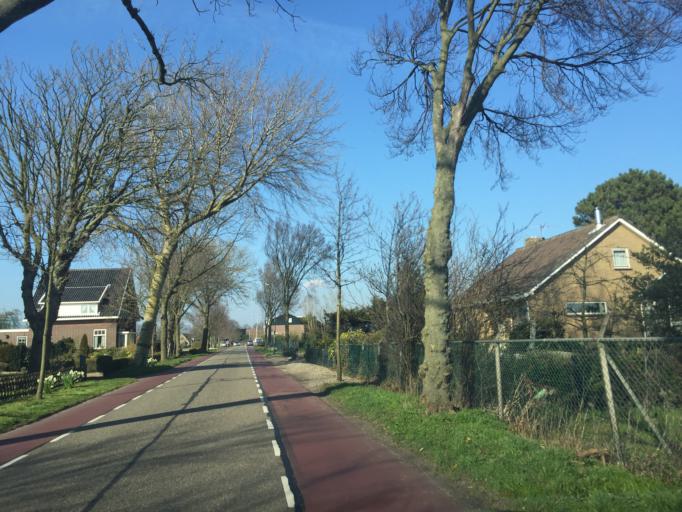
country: NL
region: South Holland
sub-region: Gemeente Hillegom
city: Hillegom
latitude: 52.3092
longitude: 4.5708
